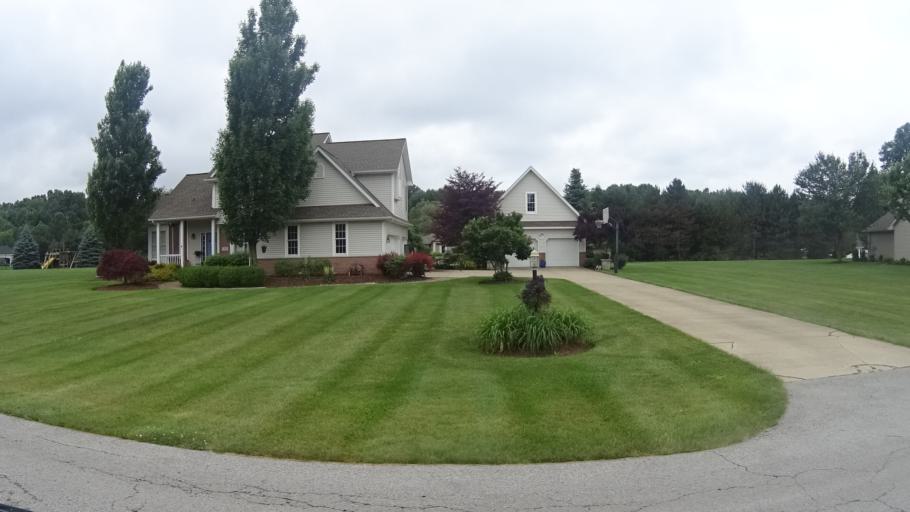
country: US
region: Ohio
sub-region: Erie County
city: Milan
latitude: 41.3011
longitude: -82.5817
